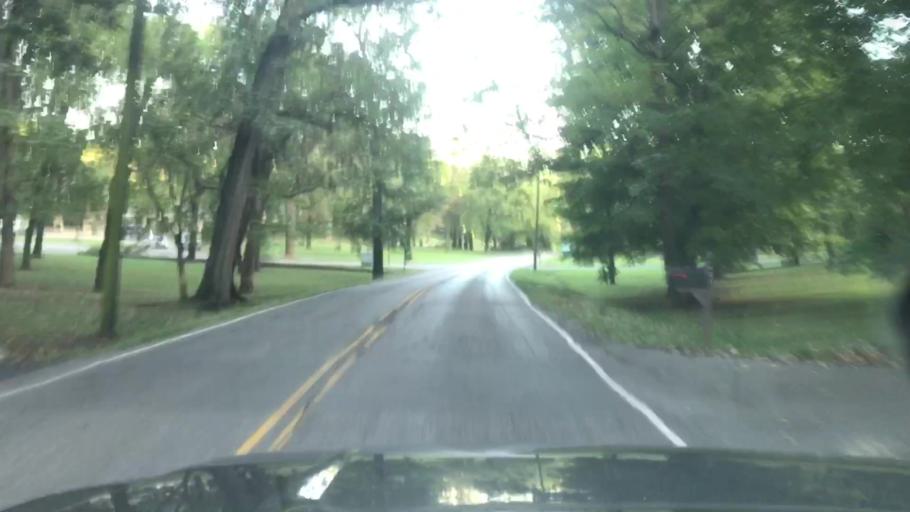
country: US
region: Tennessee
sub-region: Davidson County
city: Belle Meade
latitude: 36.1303
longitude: -86.8651
